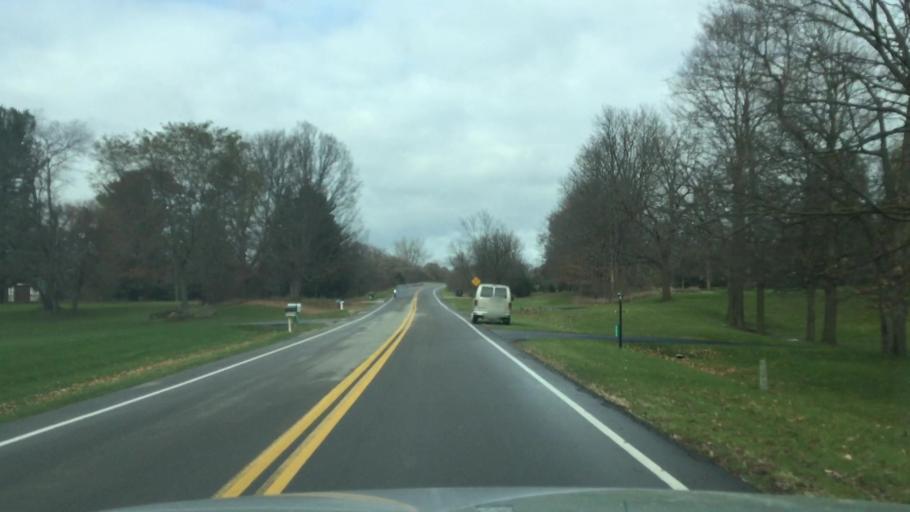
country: US
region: Michigan
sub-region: Washtenaw County
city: Ypsilanti
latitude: 42.3230
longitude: -83.6450
